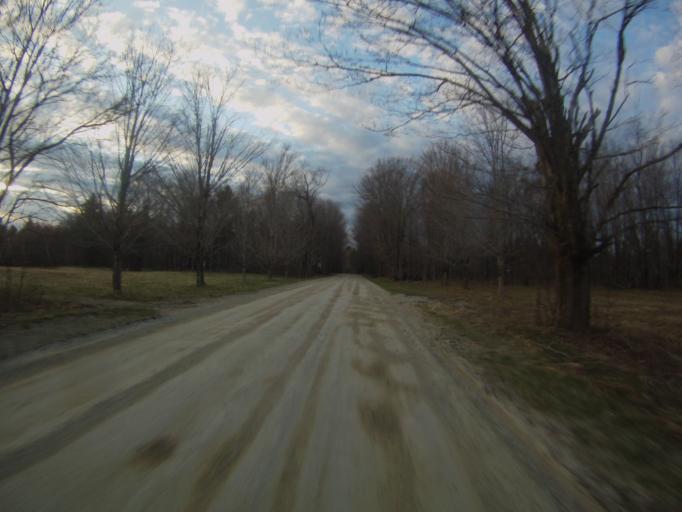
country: US
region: Vermont
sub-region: Rutland County
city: Brandon
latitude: 43.8969
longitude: -73.0132
